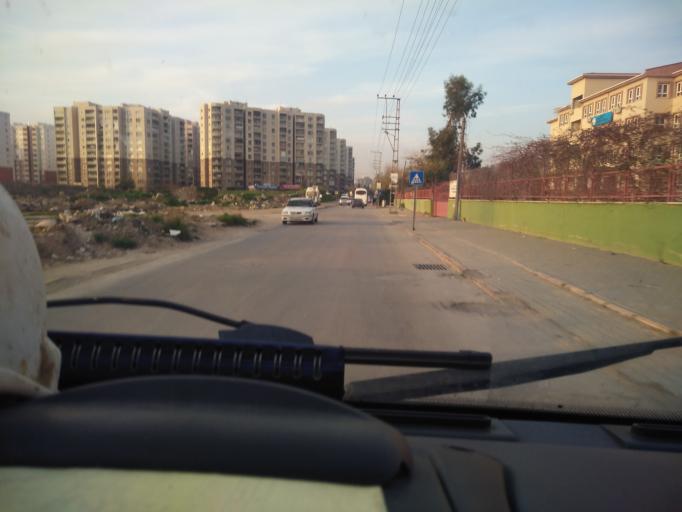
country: TR
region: Adana
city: Seyhan
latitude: 37.0053
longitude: 35.2800
